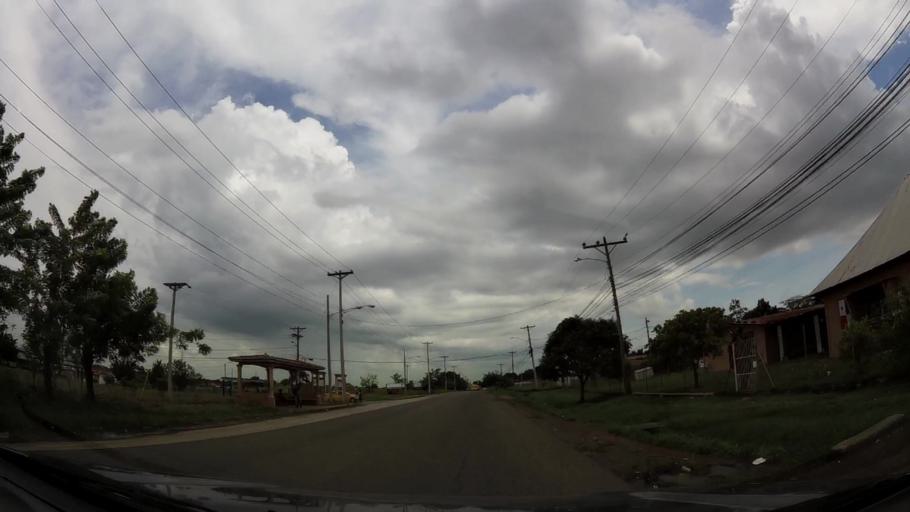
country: PA
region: Panama
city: Cabra Numero Uno
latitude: 9.1124
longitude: -79.3267
